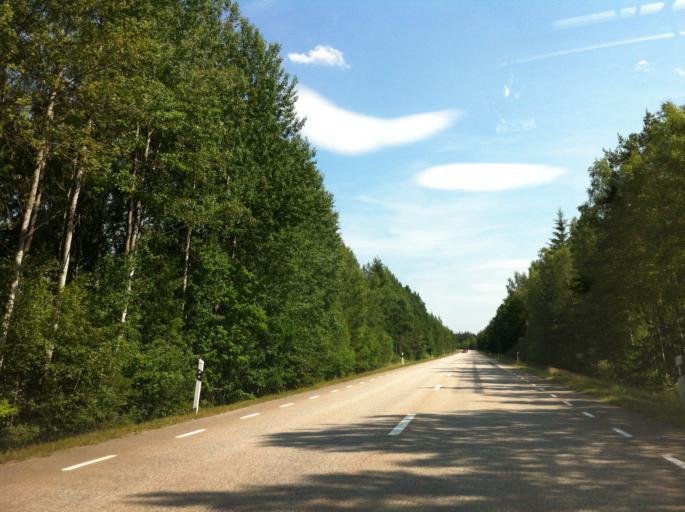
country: SE
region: Kalmar
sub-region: Nybro Kommun
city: Nybro
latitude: 56.8305
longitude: 15.7449
